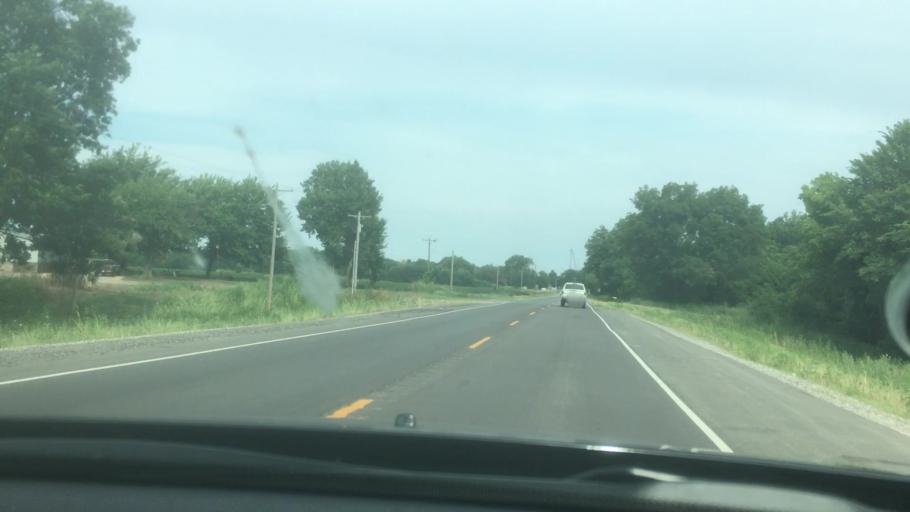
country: US
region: Oklahoma
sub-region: Garvin County
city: Maysville
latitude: 34.8157
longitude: -97.3953
